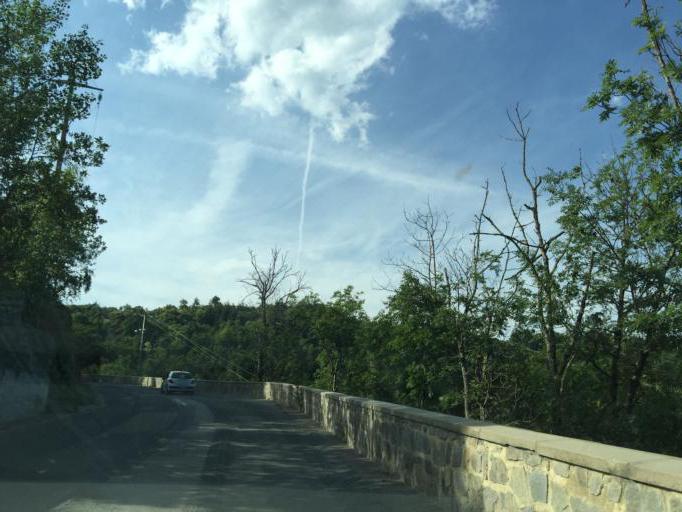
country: FR
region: Rhone-Alpes
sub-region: Departement de la Loire
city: Saint-Julien-Molin-Molette
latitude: 45.3310
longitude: 4.6034
